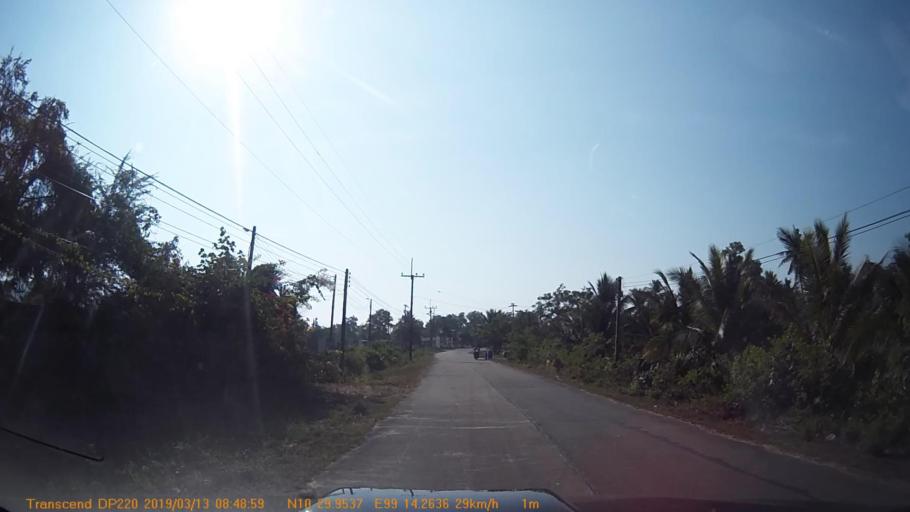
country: TH
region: Chumphon
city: Chumphon
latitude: 10.4991
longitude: 99.2379
